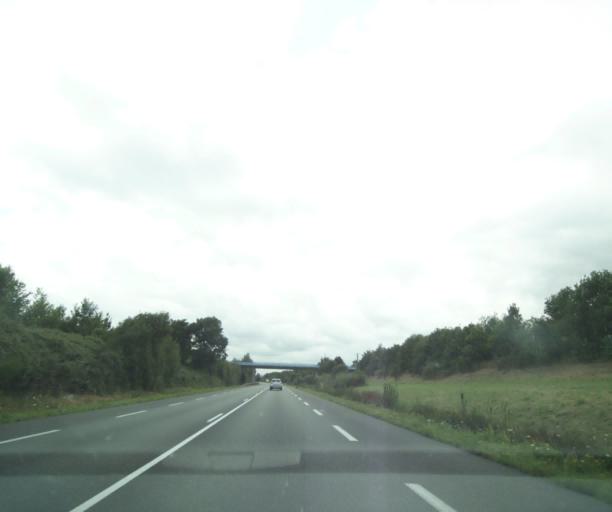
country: FR
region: Pays de la Loire
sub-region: Departement de la Vendee
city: Les Clouzeaux
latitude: 46.6552
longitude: -1.4994
